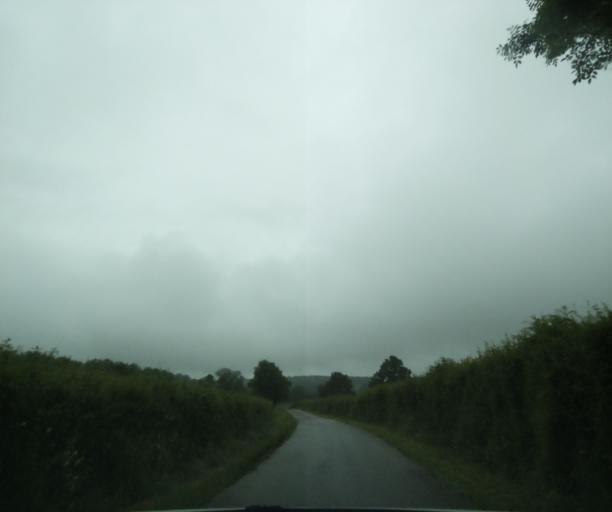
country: FR
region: Bourgogne
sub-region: Departement de Saone-et-Loire
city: Charolles
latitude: 46.4515
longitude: 4.2098
